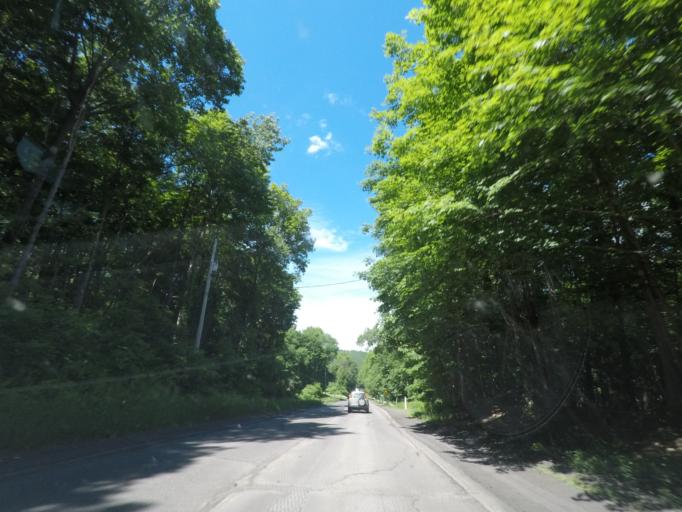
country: US
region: Massachusetts
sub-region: Berkshire County
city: West Stockbridge
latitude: 42.3422
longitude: -73.4160
